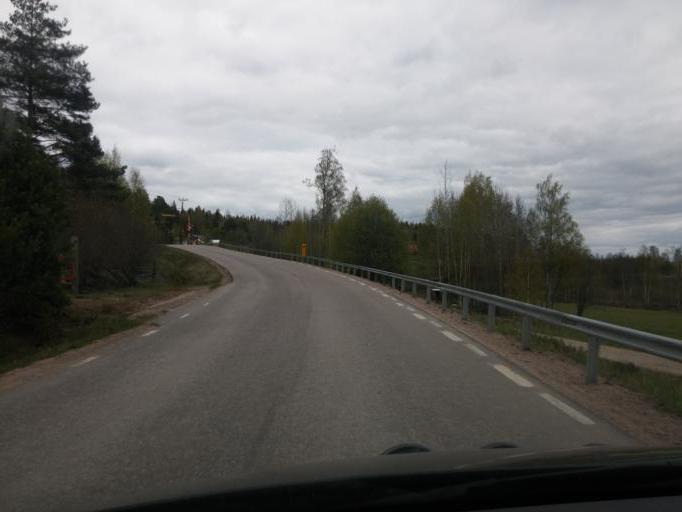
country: SE
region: Gaevleborg
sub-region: Ljusdals Kommun
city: Ljusdal
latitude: 61.8562
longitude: 16.0350
